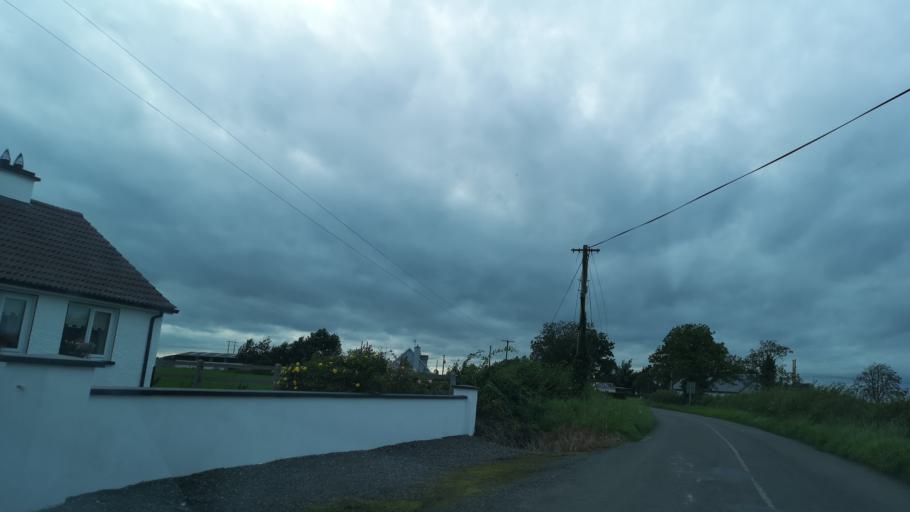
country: IE
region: Leinster
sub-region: Uibh Fhaili
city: Ferbane
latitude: 53.2200
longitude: -7.7993
